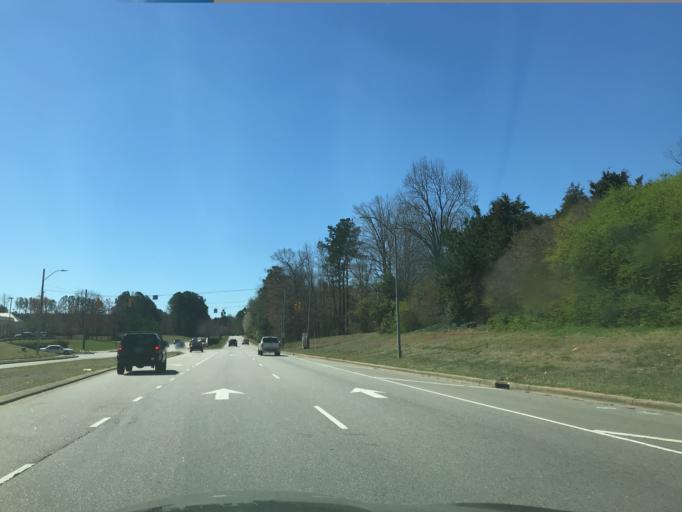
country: US
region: North Carolina
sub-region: Wake County
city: Garner
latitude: 35.7154
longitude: -78.6401
